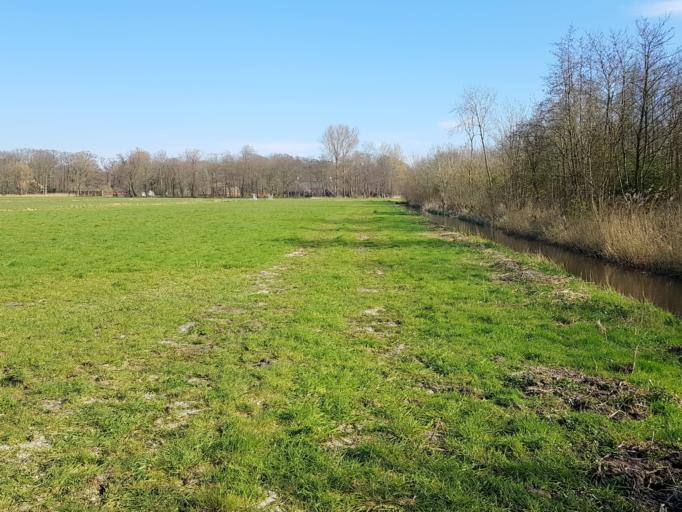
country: NL
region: South Holland
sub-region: Gemeente Lisse
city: Lisse
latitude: 52.2691
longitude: 4.5338
